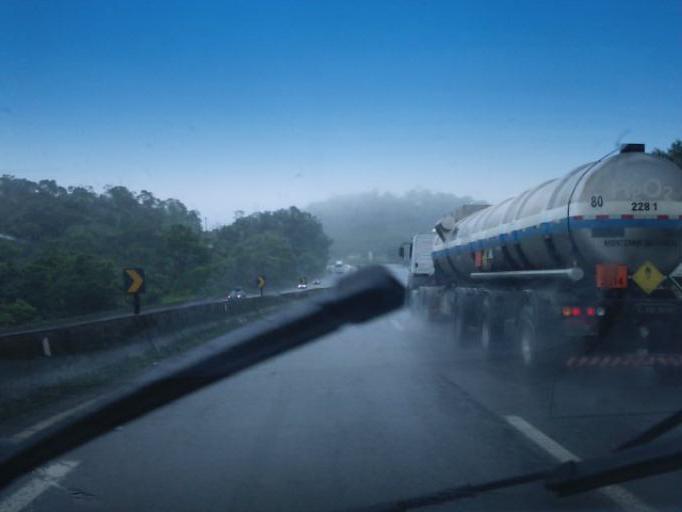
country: BR
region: Parana
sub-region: Antonina
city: Antonina
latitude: -25.1111
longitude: -48.7534
